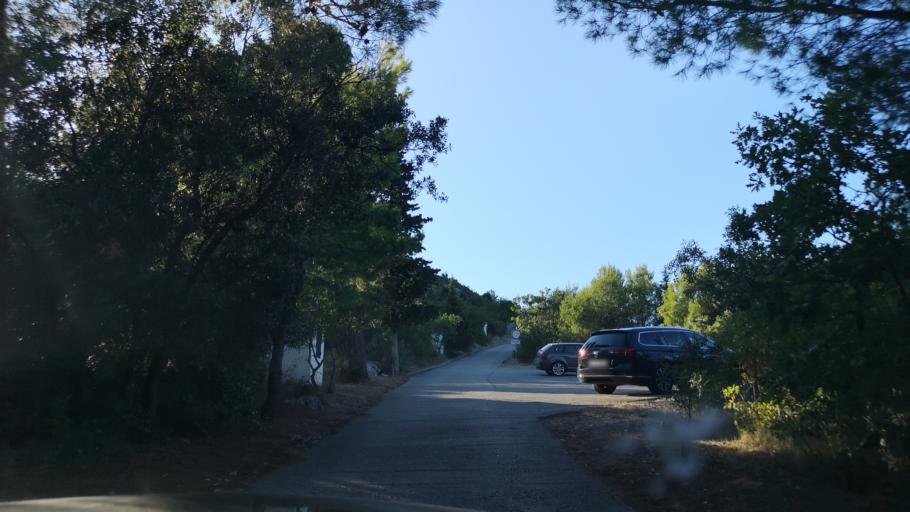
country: HR
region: Sibensko-Kniniska
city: Vodice
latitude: 43.7846
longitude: 15.7714
